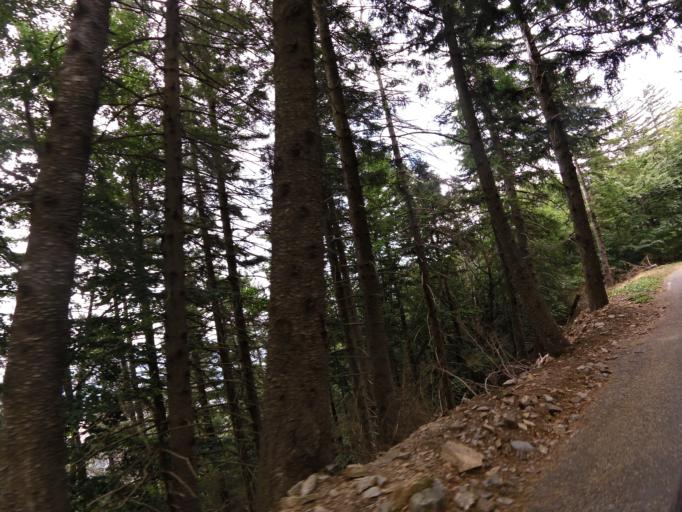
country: FR
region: Languedoc-Roussillon
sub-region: Departement du Gard
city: Valleraugue
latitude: 44.0505
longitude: 3.6079
